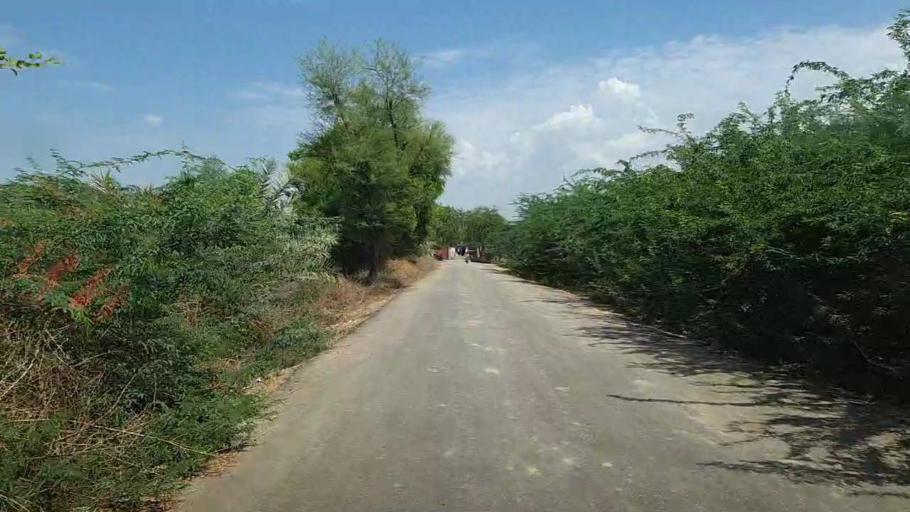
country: PK
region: Sindh
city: Bhiria
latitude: 26.9512
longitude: 68.2295
